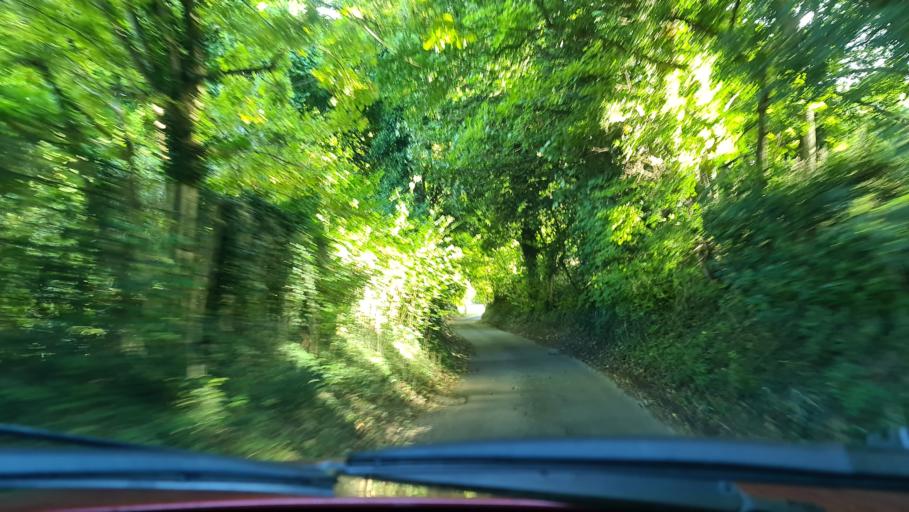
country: GB
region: England
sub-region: Buckinghamshire
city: Princes Risborough
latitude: 51.7070
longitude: -0.8189
